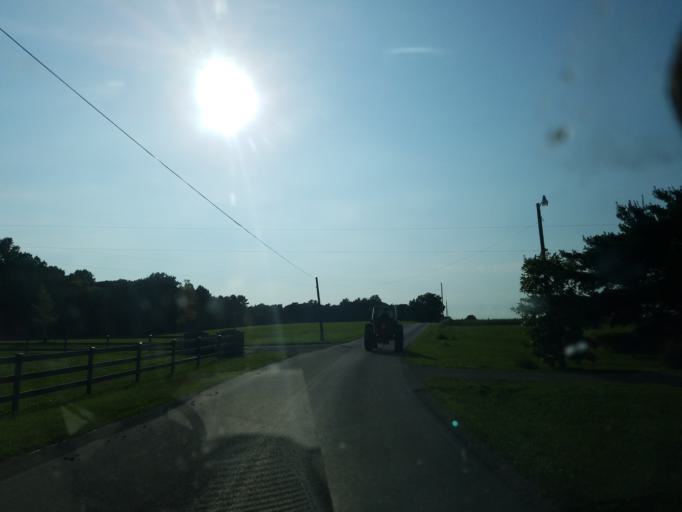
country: US
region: Ohio
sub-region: Adams County
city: West Union
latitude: 38.8841
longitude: -83.5028
